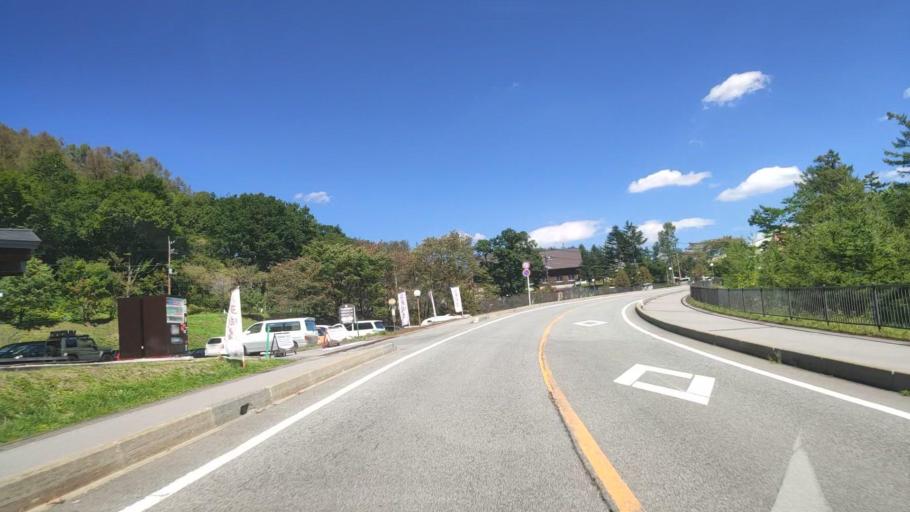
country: JP
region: Nagano
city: Nakano
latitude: 36.6264
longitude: 138.5856
